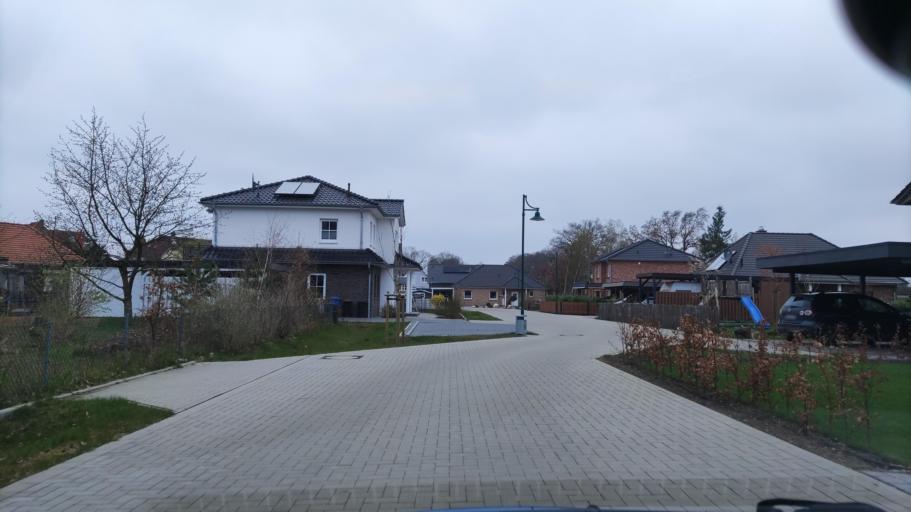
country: DE
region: Lower Saxony
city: Wulfsen
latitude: 53.2978
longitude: 10.1410
